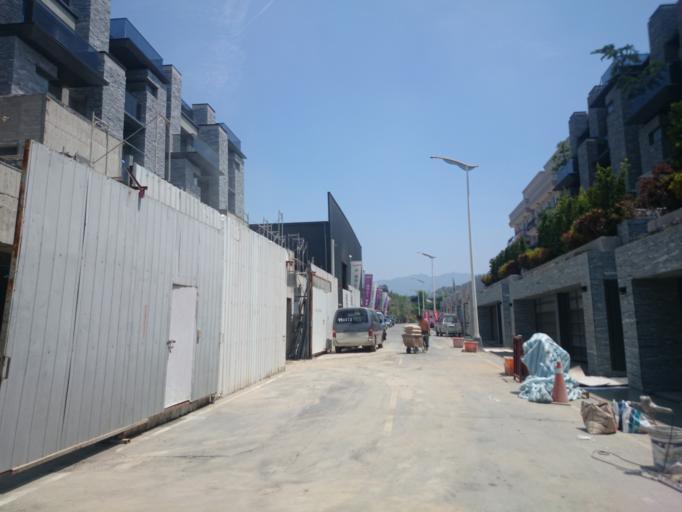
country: TW
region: Taiwan
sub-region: Taichung City
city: Taichung
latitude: 24.1760
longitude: 120.7280
